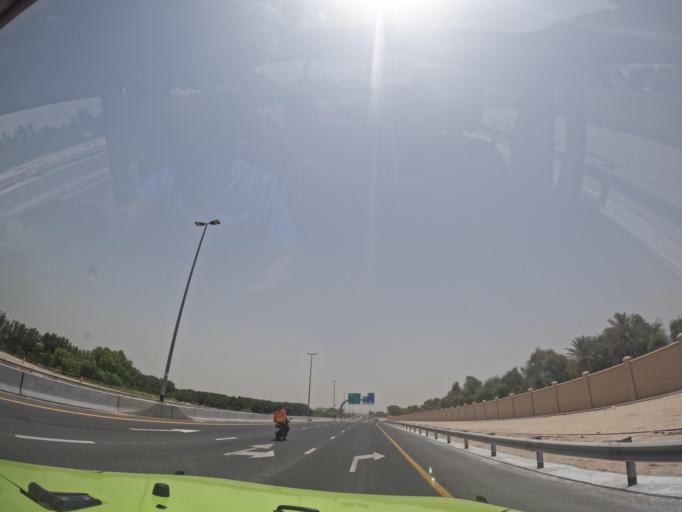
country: AE
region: Dubai
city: Dubai
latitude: 25.1475
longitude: 55.3270
